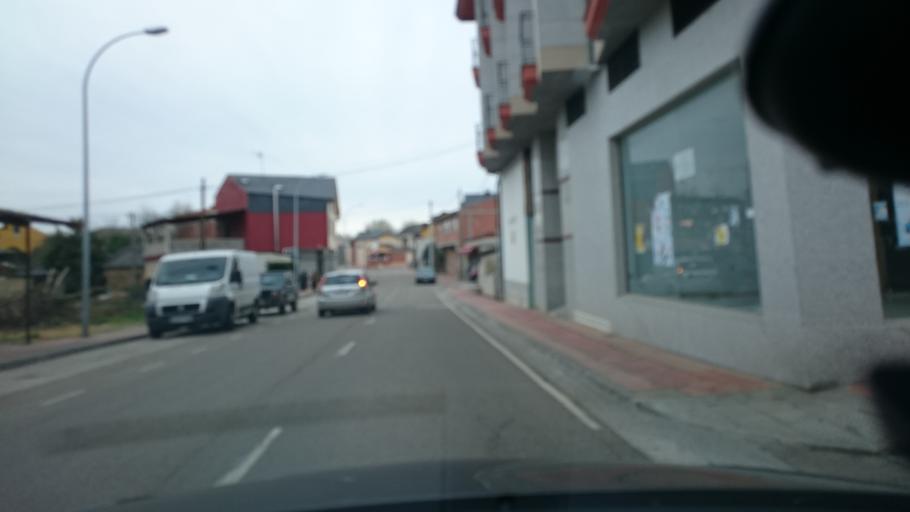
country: ES
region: Castille and Leon
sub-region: Provincia de Leon
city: Carracedelo
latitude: 42.5563
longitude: -6.7310
